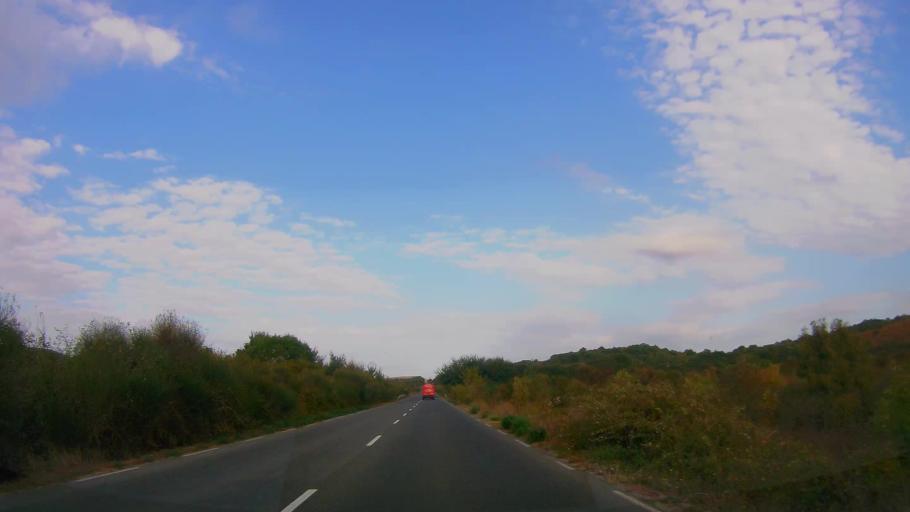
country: BG
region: Burgas
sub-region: Obshtina Sozopol
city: Sozopol
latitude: 42.3649
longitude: 27.6946
